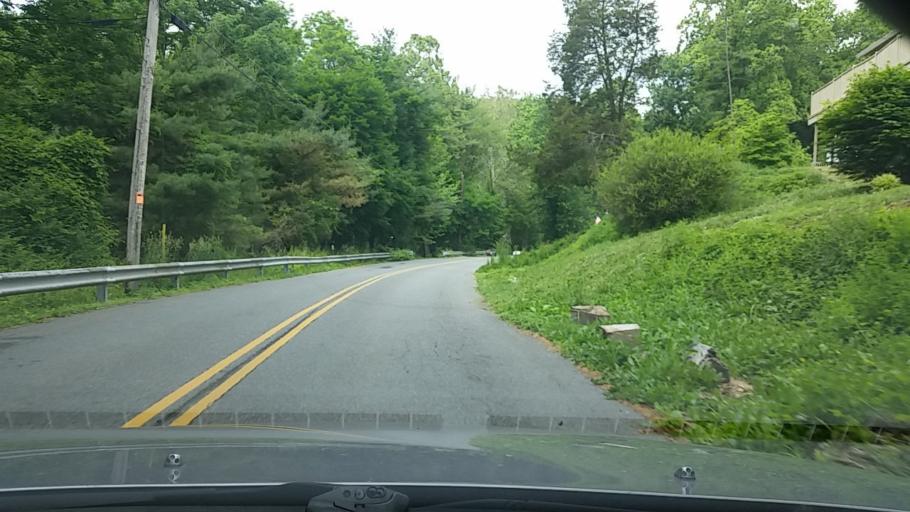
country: US
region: New Jersey
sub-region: Warren County
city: Oxford
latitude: 40.8609
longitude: -74.9795
